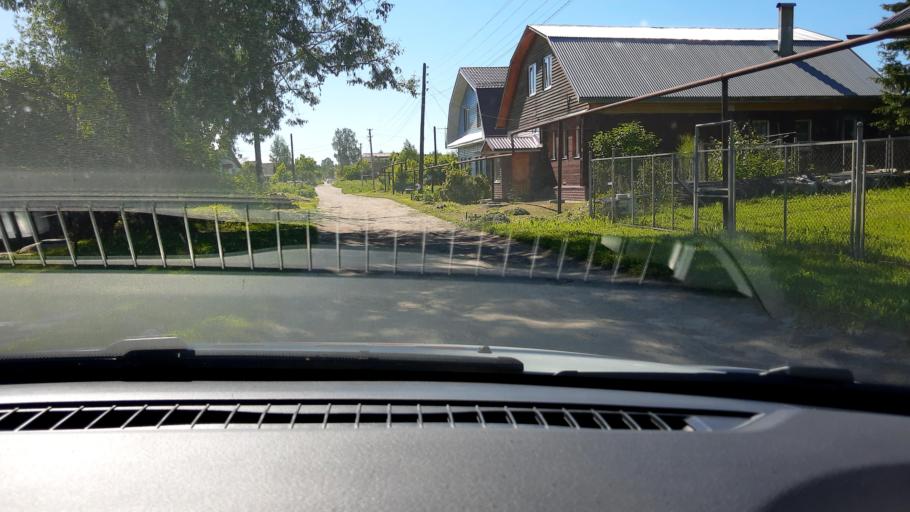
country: RU
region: Nizjnij Novgorod
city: Bor
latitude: 56.3942
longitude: 44.0472
